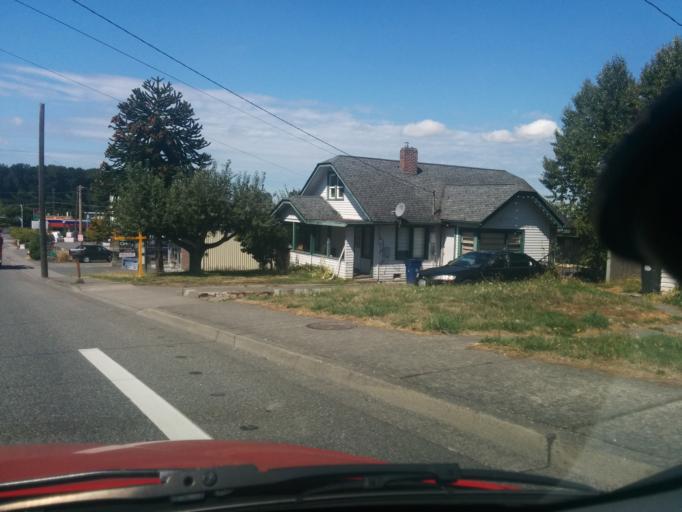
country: US
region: Washington
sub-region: Skagit County
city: Mount Vernon
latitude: 48.4286
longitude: -122.3329
